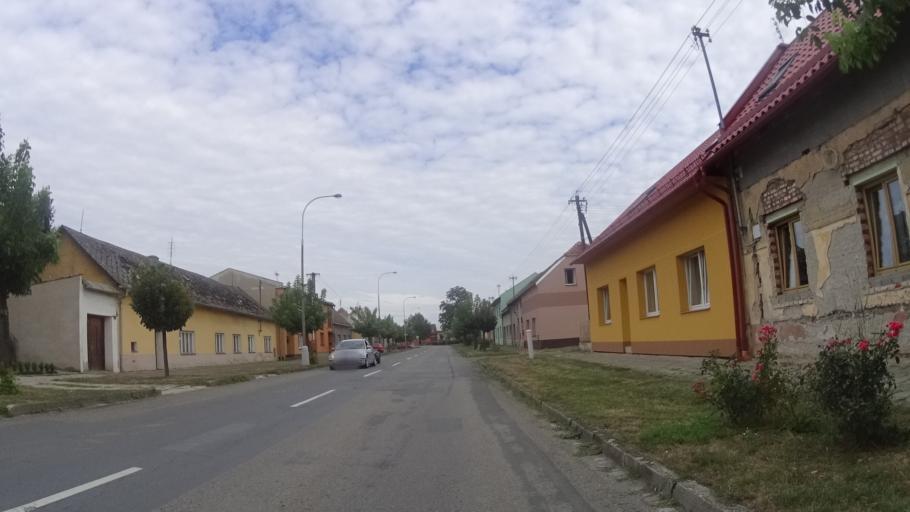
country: CZ
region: Olomoucky
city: Tovacov
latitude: 49.4341
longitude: 17.2865
